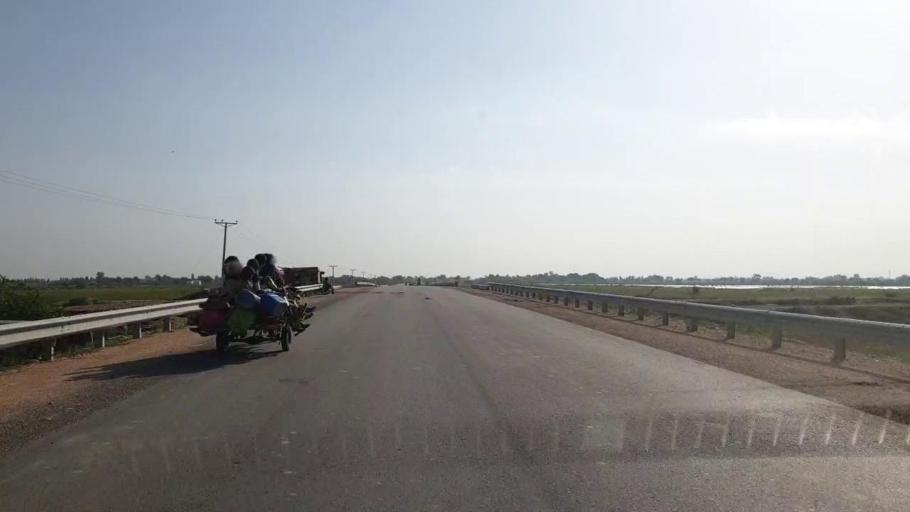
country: PK
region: Sindh
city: Tando Bago
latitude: 24.6568
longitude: 69.0190
